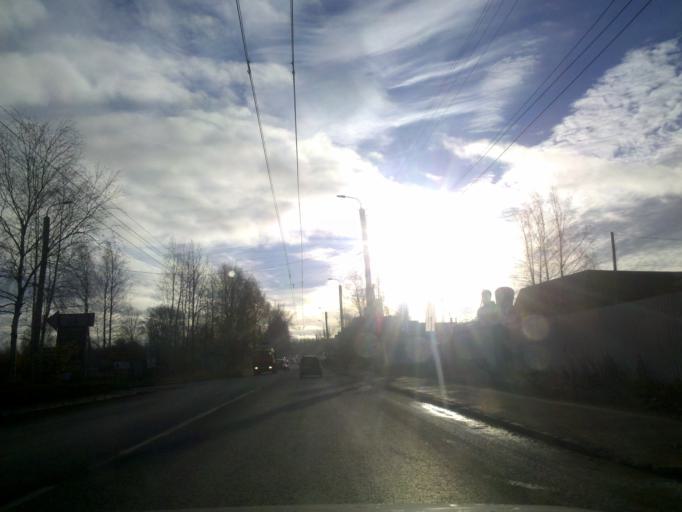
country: RU
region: Republic of Karelia
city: Petrozavodsk
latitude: 61.7760
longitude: 34.4133
